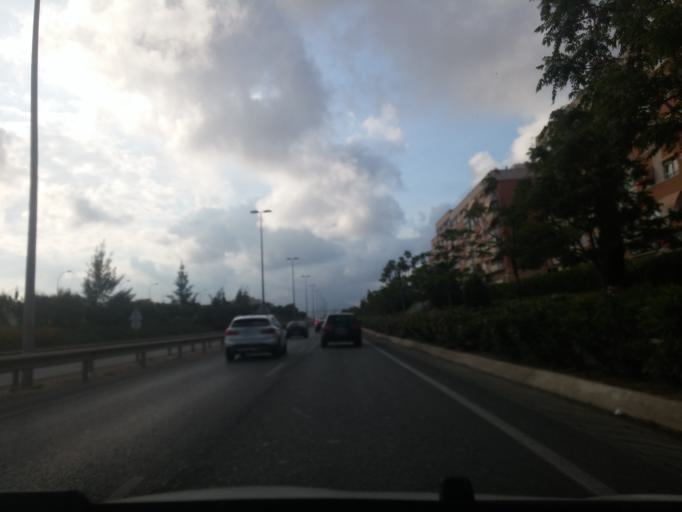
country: ES
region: Valencia
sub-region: Provincia de Alicante
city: Alicante
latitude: 38.3662
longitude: -0.5007
